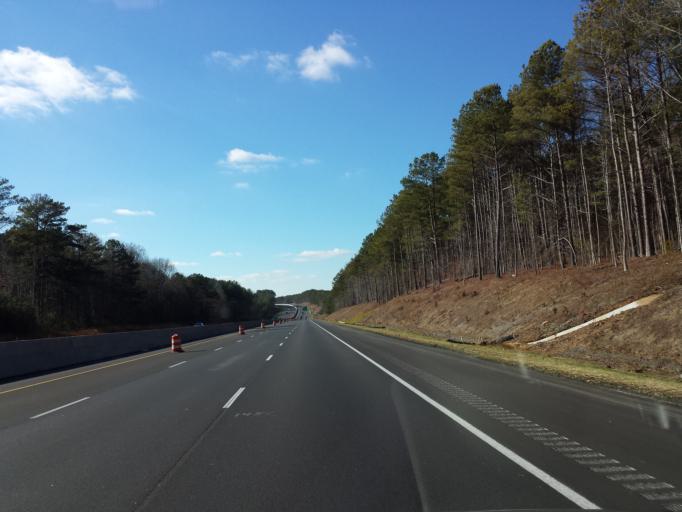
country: US
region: Alabama
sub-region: Cleburne County
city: Heflin
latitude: 33.6466
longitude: -85.4744
